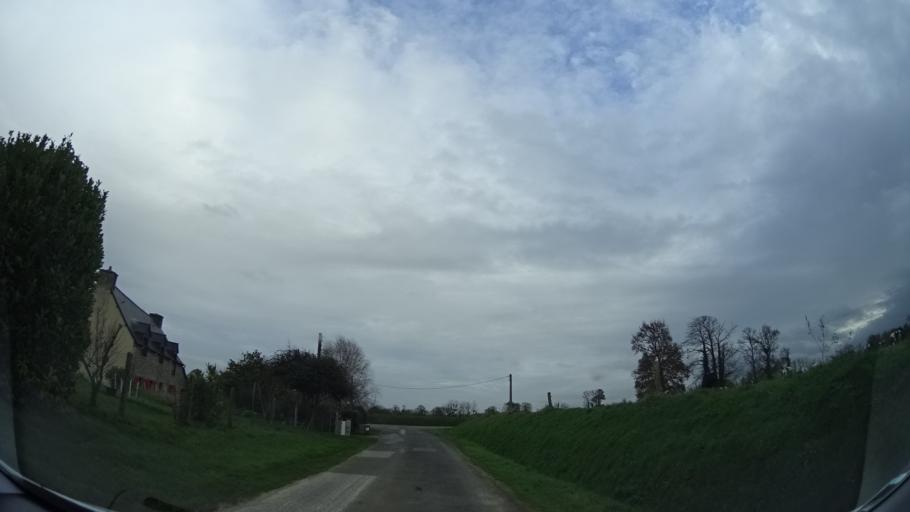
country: FR
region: Brittany
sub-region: Departement des Cotes-d'Armor
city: Evran
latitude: 48.3335
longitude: -1.9497
